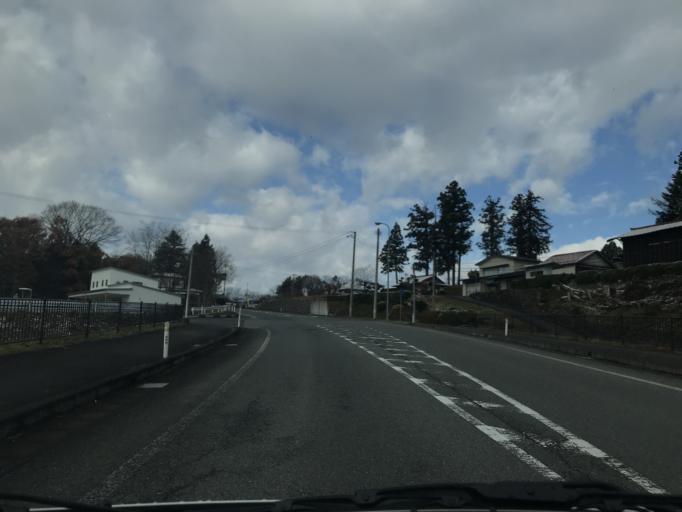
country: JP
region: Iwate
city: Mizusawa
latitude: 39.1084
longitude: 141.1382
